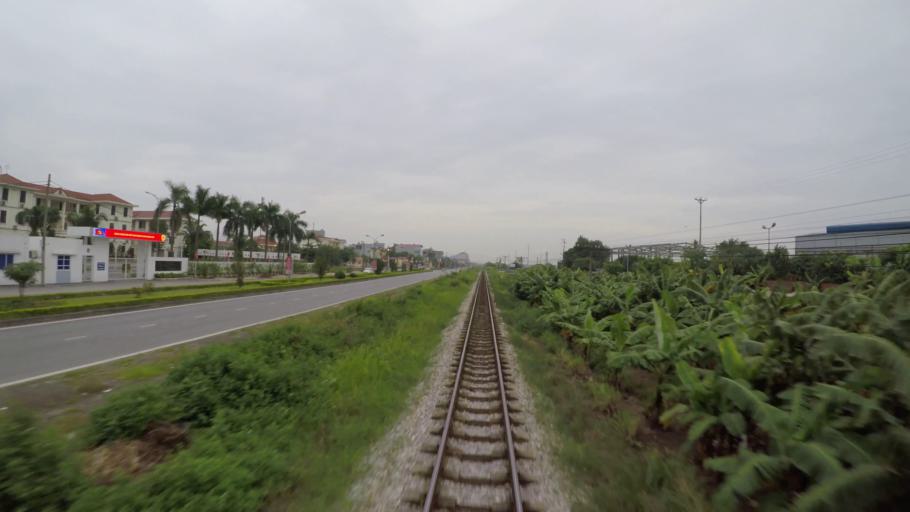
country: VN
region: Hung Yen
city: Nhu Quynh
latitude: 20.9809
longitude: 106.0230
